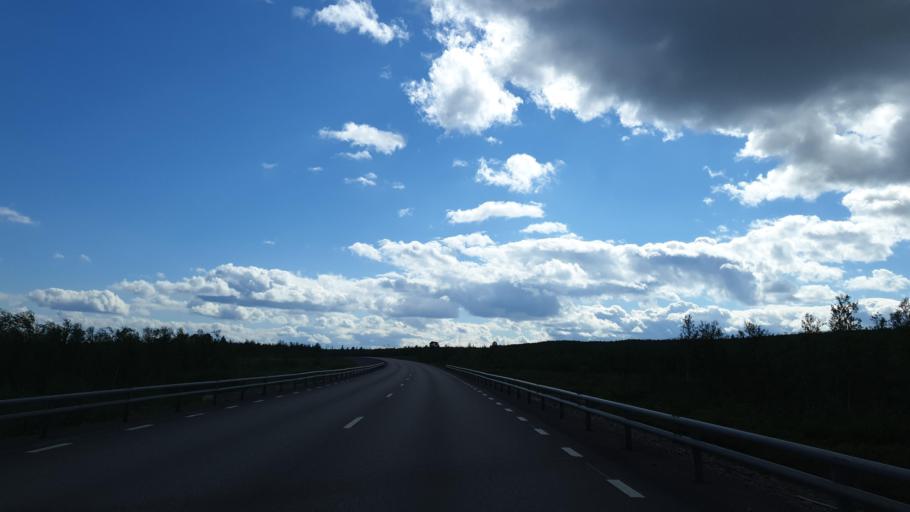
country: SE
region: Norrbotten
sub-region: Kiruna Kommun
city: Kiruna
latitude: 67.8162
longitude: 20.2442
